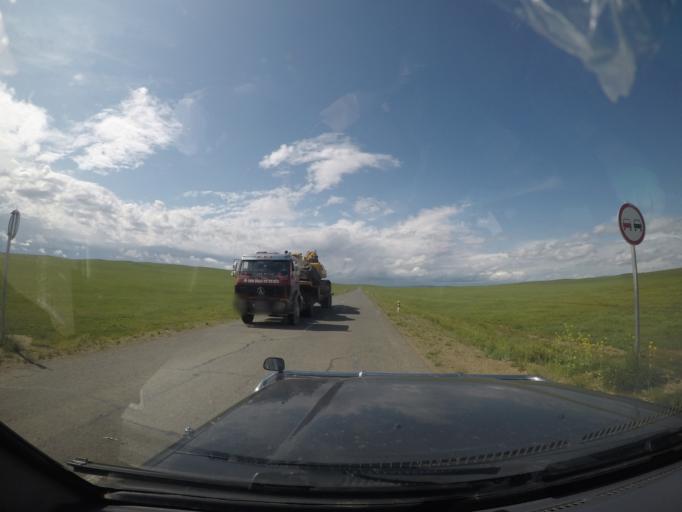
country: MN
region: Hentiy
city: Bayanbulag
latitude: 47.4406
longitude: 109.7183
